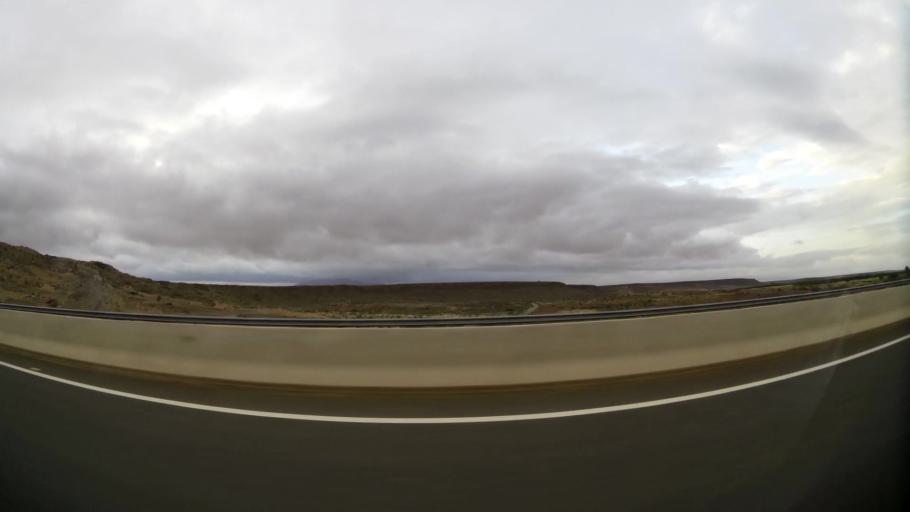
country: MA
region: Taza-Al Hoceima-Taounate
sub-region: Taza
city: Guercif
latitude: 34.3931
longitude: -3.2122
